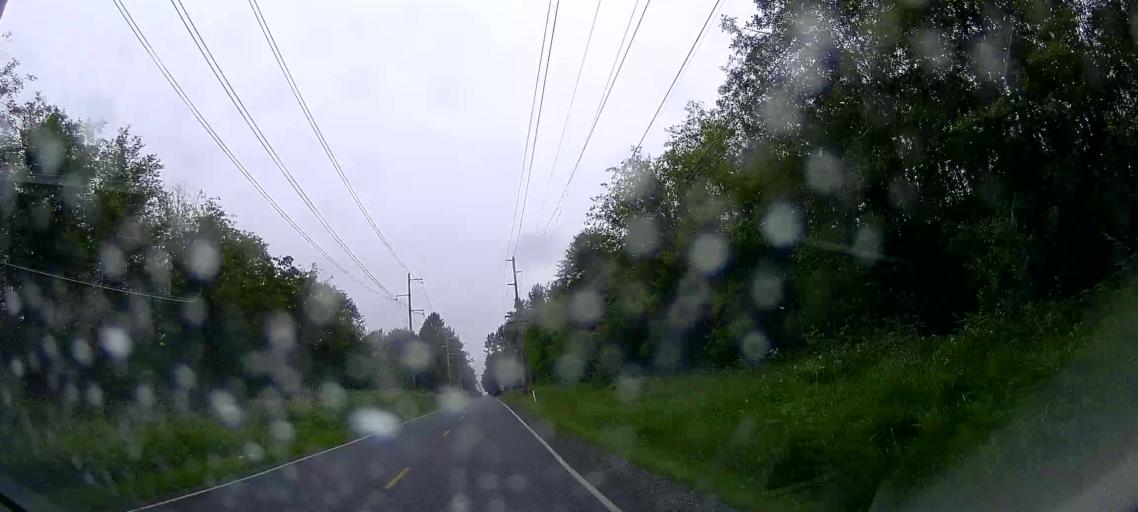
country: US
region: Washington
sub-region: Whatcom County
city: Birch Bay
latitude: 48.8752
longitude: -122.7042
